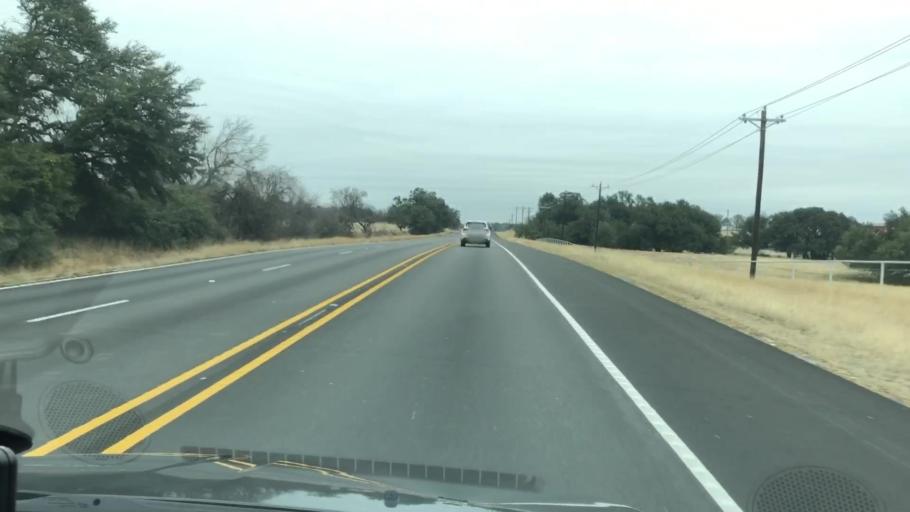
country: US
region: Texas
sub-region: Erath County
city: Stephenville
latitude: 32.3062
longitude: -98.1860
